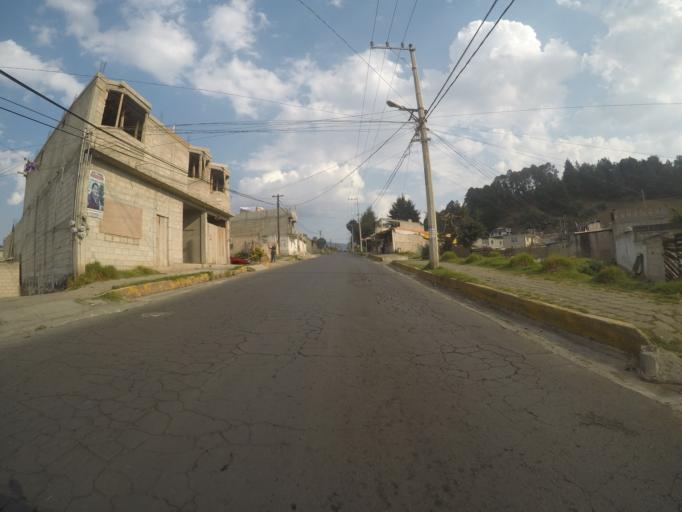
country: MX
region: Mexico
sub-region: Xalatlaco
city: El Aguila (La Mesa)
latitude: 19.1706
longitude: -99.4108
